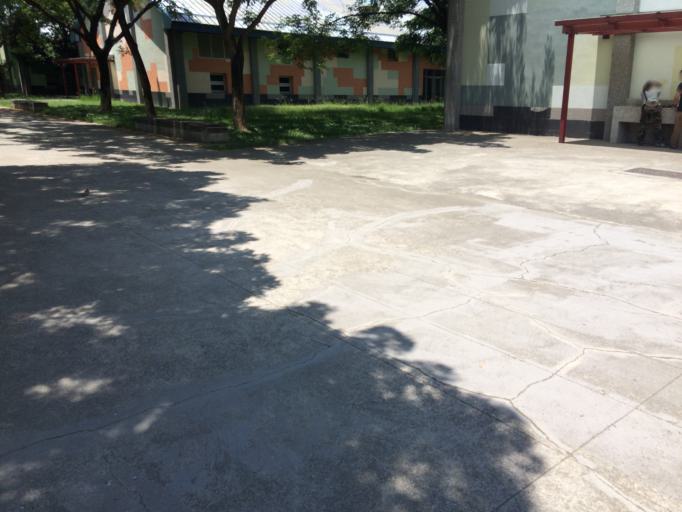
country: TW
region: Taiwan
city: Fengshan
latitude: 22.6195
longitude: 120.3395
